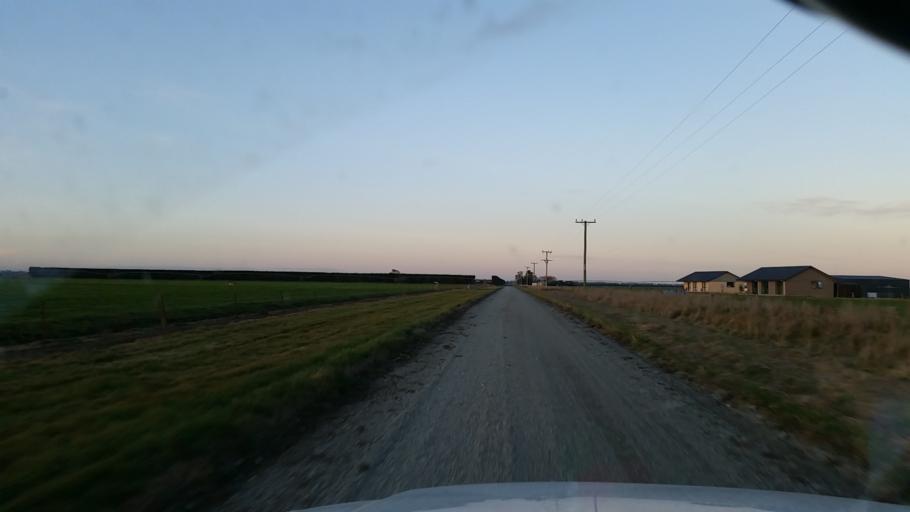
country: NZ
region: Canterbury
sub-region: Ashburton District
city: Tinwald
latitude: -43.9524
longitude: 171.5660
